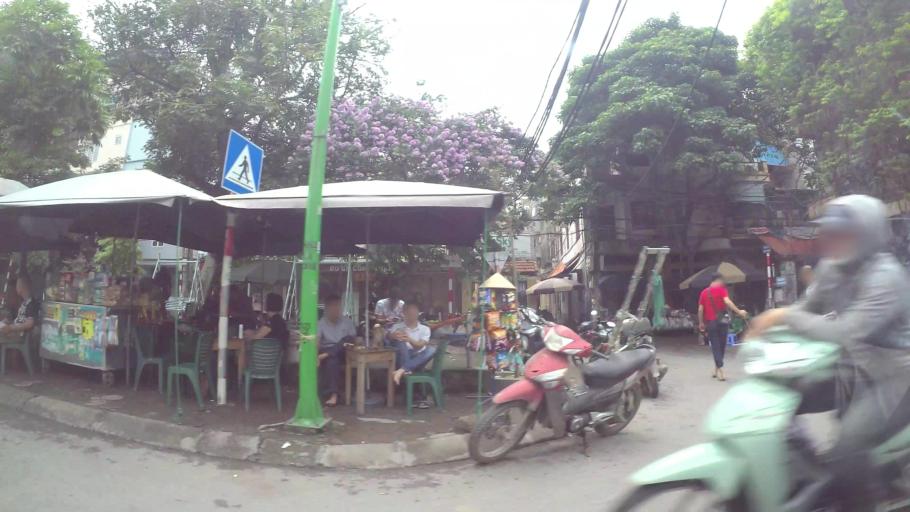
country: VN
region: Ha Noi
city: Hai BaTrung
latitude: 20.9815
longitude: 105.8461
